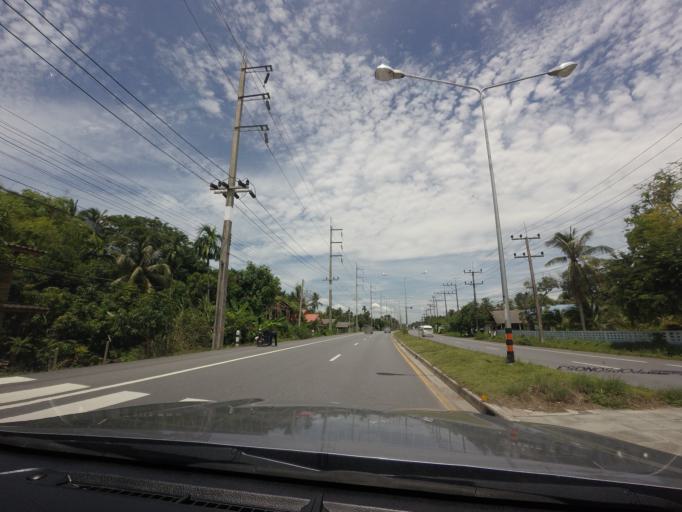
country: TH
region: Songkhla
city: Krasae Sin
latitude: 7.5756
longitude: 100.4091
